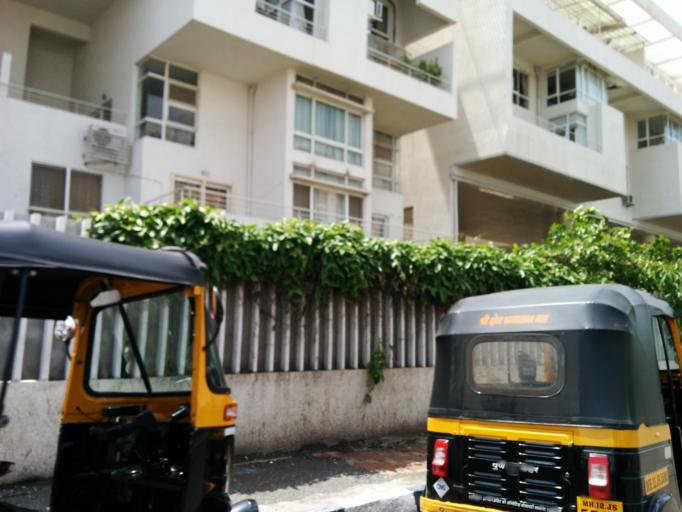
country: IN
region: Maharashtra
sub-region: Pune Division
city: Lohogaon
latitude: 18.5729
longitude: 73.9074
